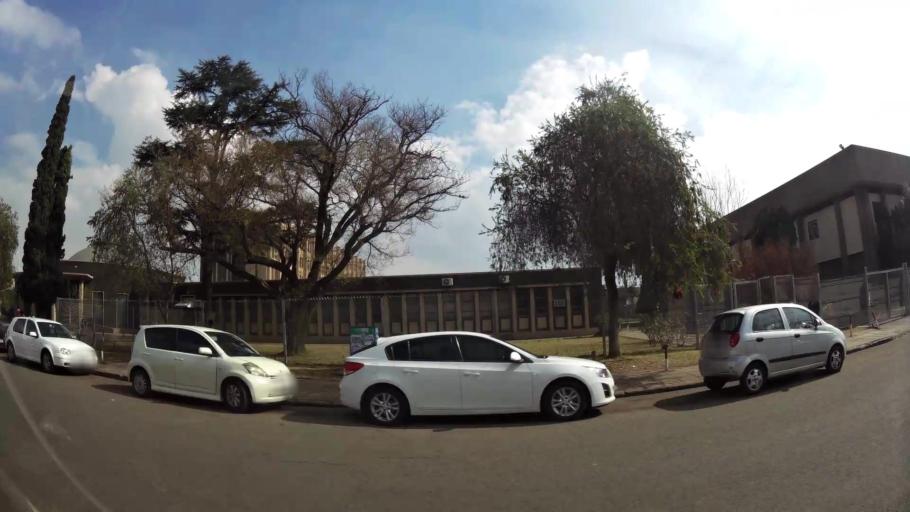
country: ZA
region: Gauteng
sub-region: Sedibeng District Municipality
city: Vereeniging
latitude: -26.6754
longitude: 27.9292
